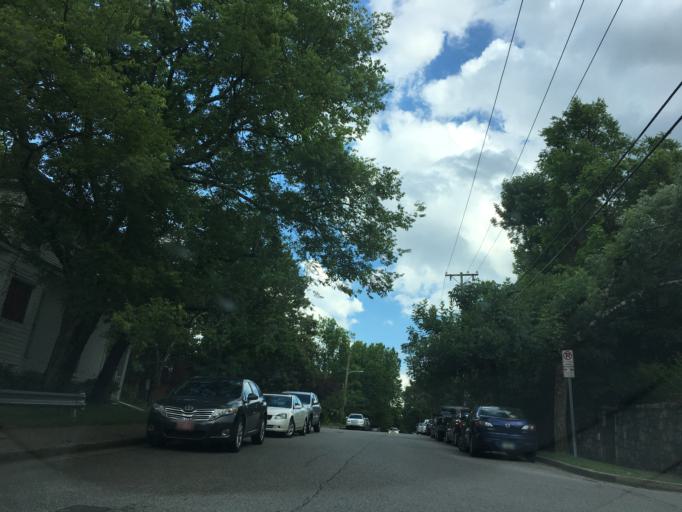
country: US
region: Tennessee
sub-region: Davidson County
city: Nashville
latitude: 36.1404
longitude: -86.8150
